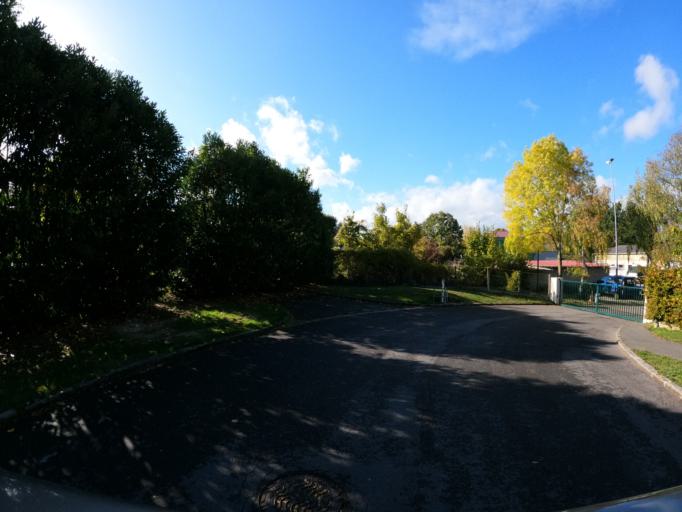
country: FR
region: Ile-de-France
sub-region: Departement de Seine-et-Marne
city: Esbly
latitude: 48.8966
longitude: 2.8082
